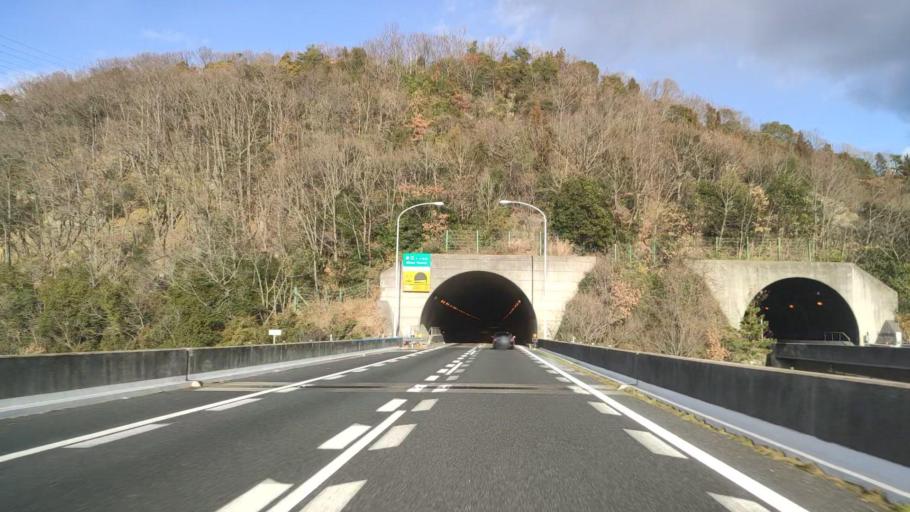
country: JP
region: Okayama
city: Kurashiki
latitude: 34.6073
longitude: 133.7290
